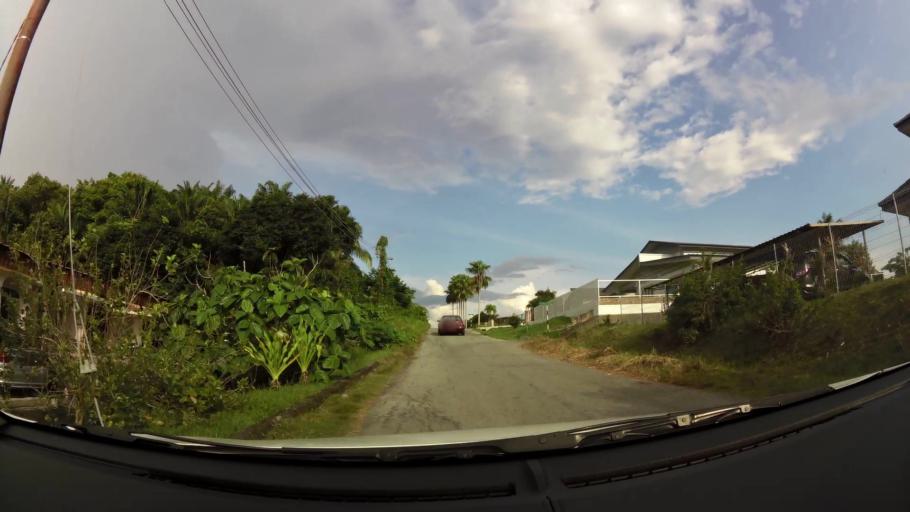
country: BN
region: Brunei and Muara
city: Bandar Seri Begawan
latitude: 4.9682
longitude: 114.9811
